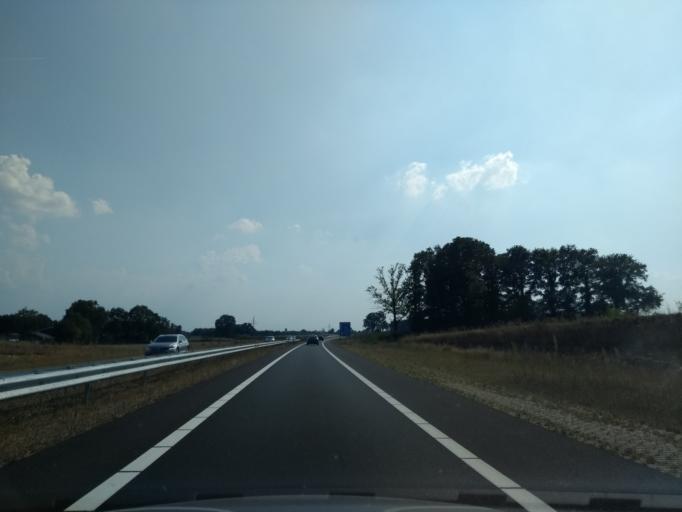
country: NL
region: Gelderland
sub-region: Berkelland
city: Eibergen
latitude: 52.1411
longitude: 6.6790
